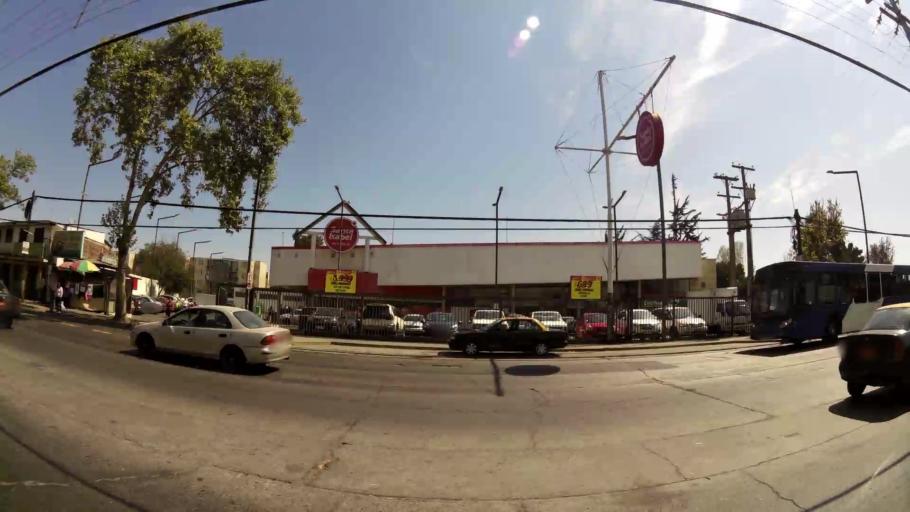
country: CL
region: Santiago Metropolitan
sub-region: Provincia de Santiago
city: La Pintana
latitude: -33.5502
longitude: -70.6719
